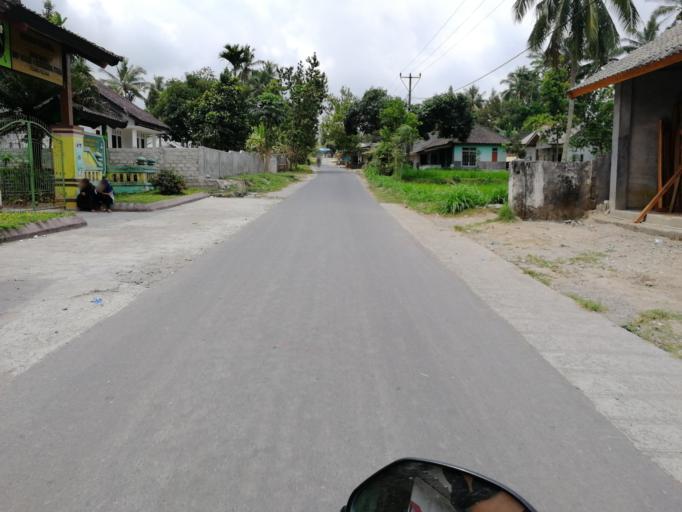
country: ID
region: West Nusa Tenggara
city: Pediti
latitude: -8.5634
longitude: 116.3312
